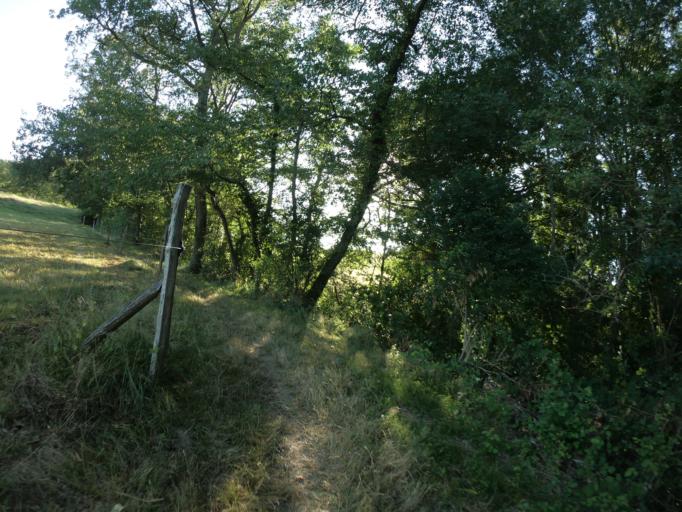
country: FR
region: Midi-Pyrenees
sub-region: Departement de l'Ariege
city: La Tour-du-Crieu
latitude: 43.1060
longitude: 1.7183
